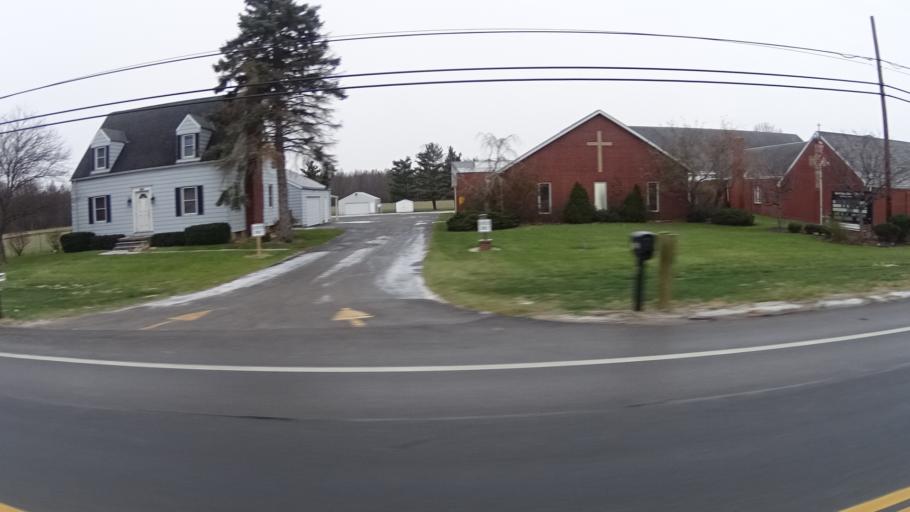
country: US
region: Ohio
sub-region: Lorain County
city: Eaton Estates
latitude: 41.3142
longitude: -82.0180
